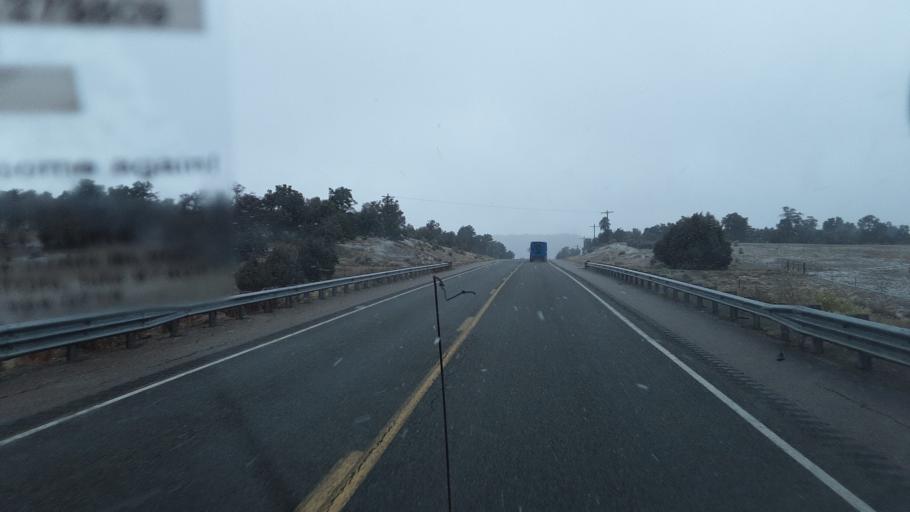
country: US
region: New Mexico
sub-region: Rio Arriba County
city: Tierra Amarilla
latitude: 36.4828
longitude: -106.4936
